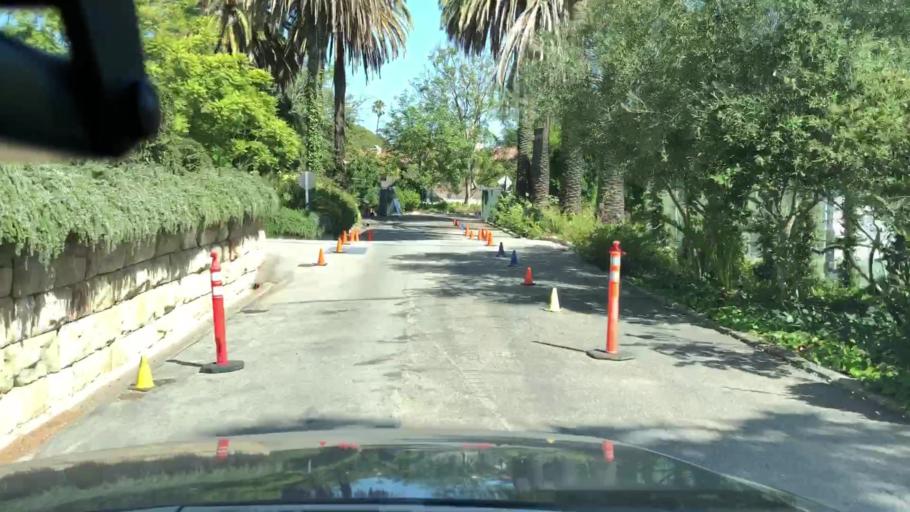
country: US
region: California
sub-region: Santa Barbara County
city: Mission Canyon
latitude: 34.4389
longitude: -119.7154
